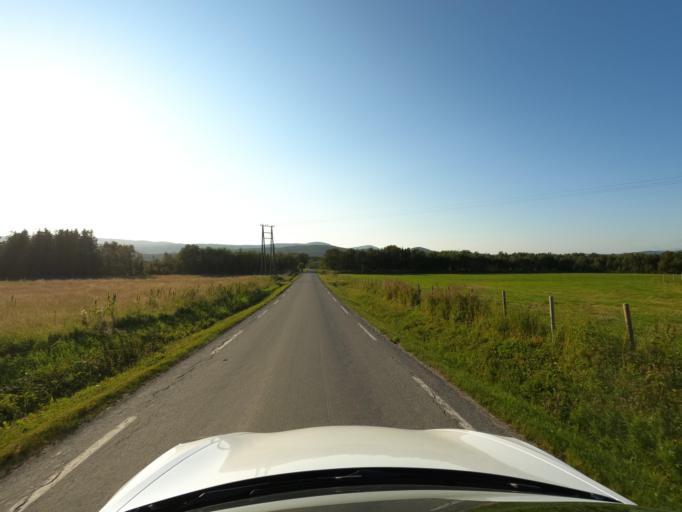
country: NO
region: Troms
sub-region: Skanland
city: Evenskjer
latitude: 68.4617
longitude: 16.6781
